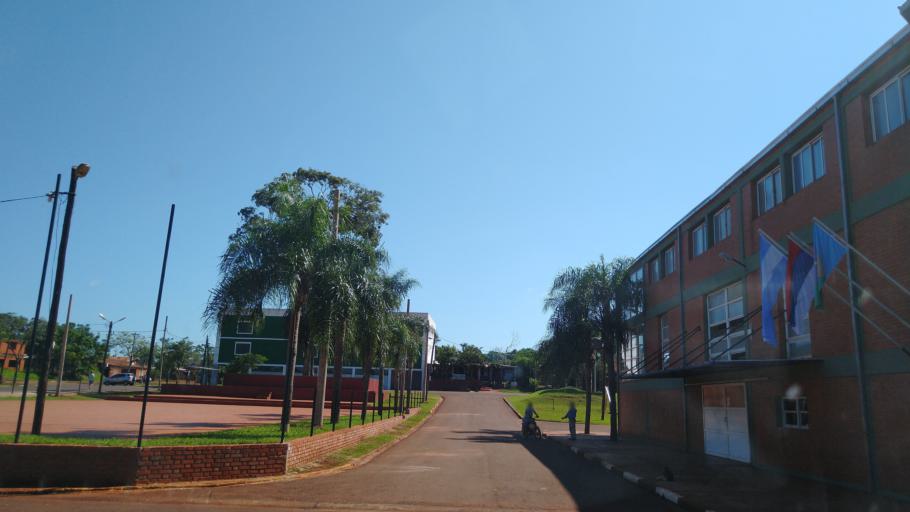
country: AR
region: Misiones
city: Puerto Libertad
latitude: -25.9652
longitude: -54.5600
